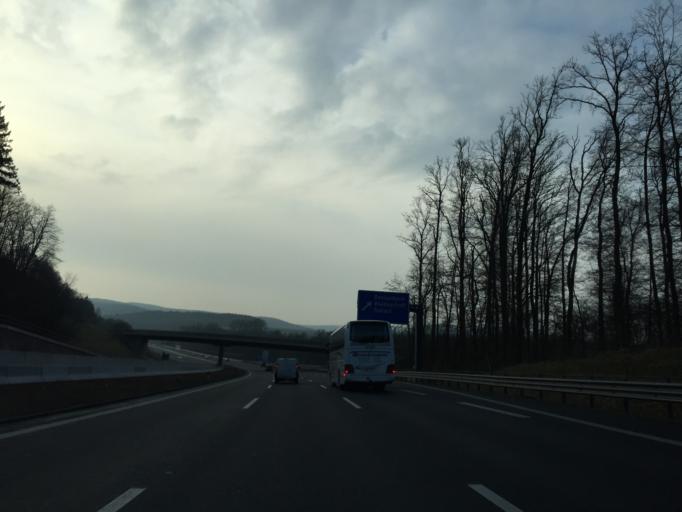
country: DE
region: Bavaria
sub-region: Regierungsbezirk Unterfranken
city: Sailauf
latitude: 49.9892
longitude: 9.2547
